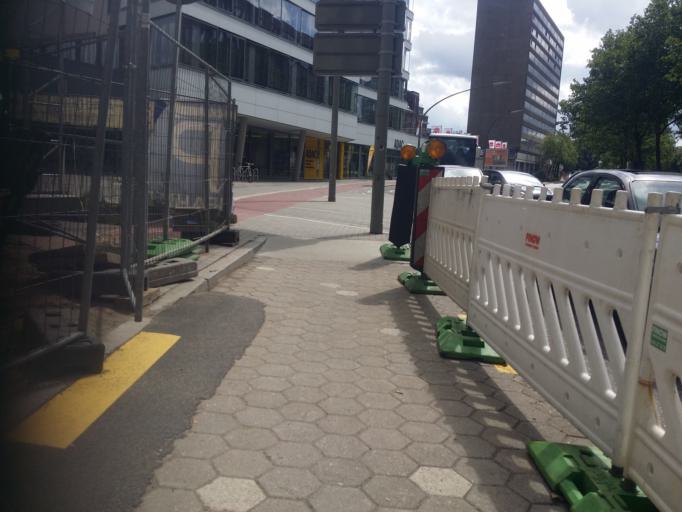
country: DE
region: Hamburg
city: Hamburg-Mitte
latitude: 53.5475
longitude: 10.0142
